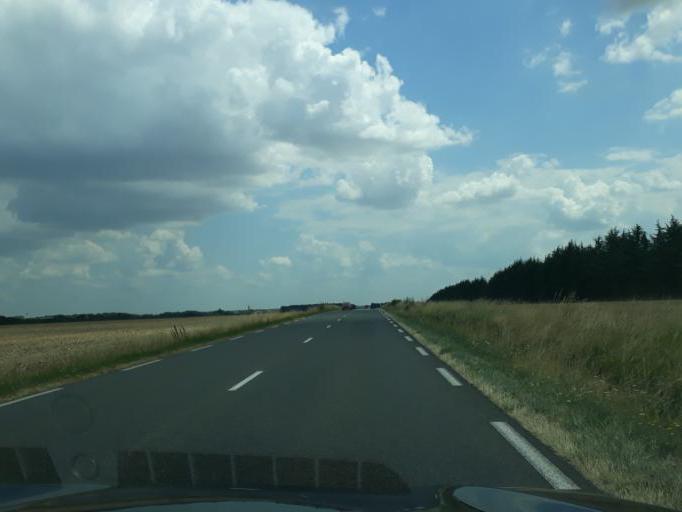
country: FR
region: Centre
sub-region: Departement du Cher
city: Avord
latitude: 47.0378
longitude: 2.5988
